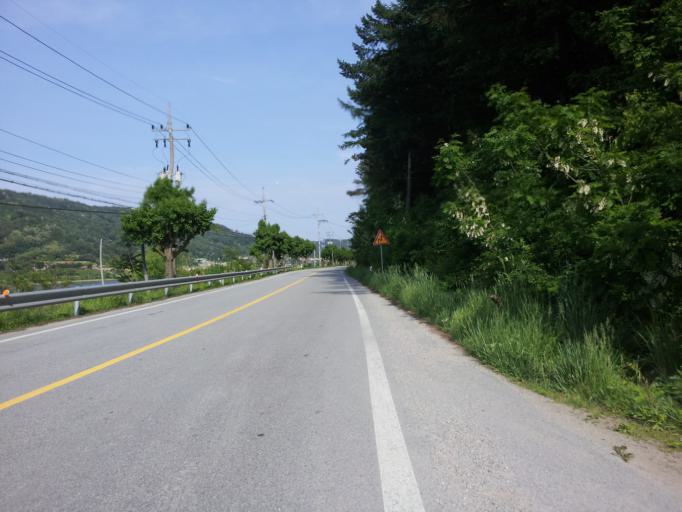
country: KR
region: Chungcheongnam-do
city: Gongju
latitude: 36.4452
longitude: 127.1804
